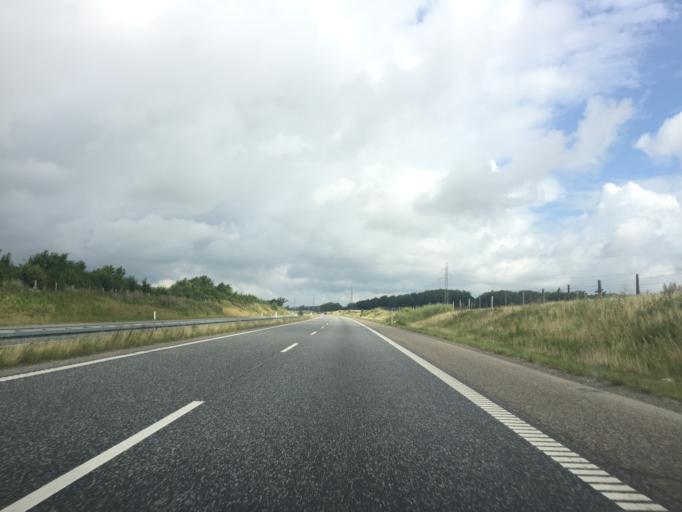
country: DK
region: South Denmark
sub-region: Svendborg Kommune
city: Svendborg
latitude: 55.1332
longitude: 10.5610
